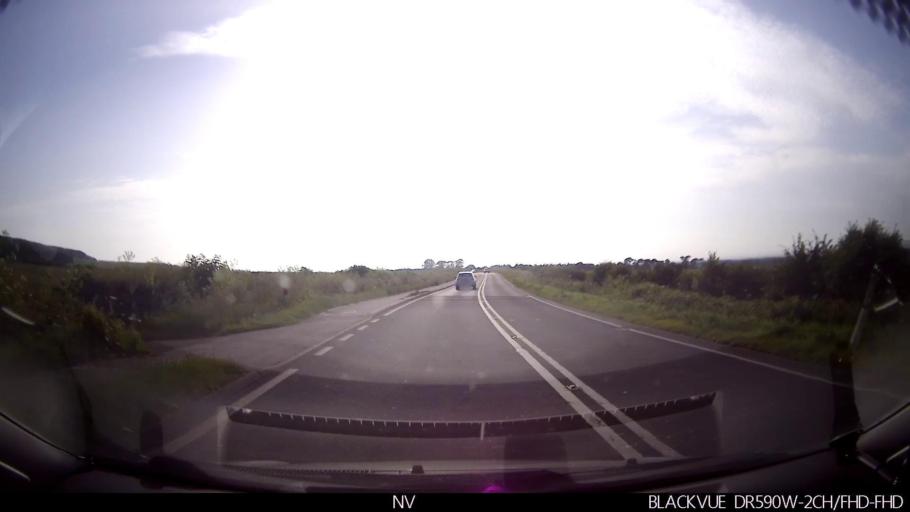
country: GB
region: England
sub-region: North Yorkshire
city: Wintringham
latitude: 54.1692
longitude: -0.6240
